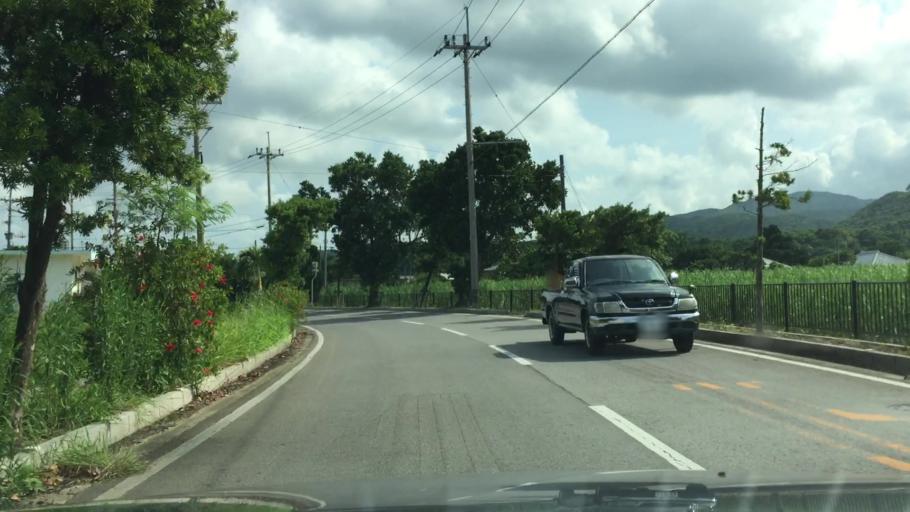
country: JP
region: Okinawa
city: Ishigaki
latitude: 24.4662
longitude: 124.2500
